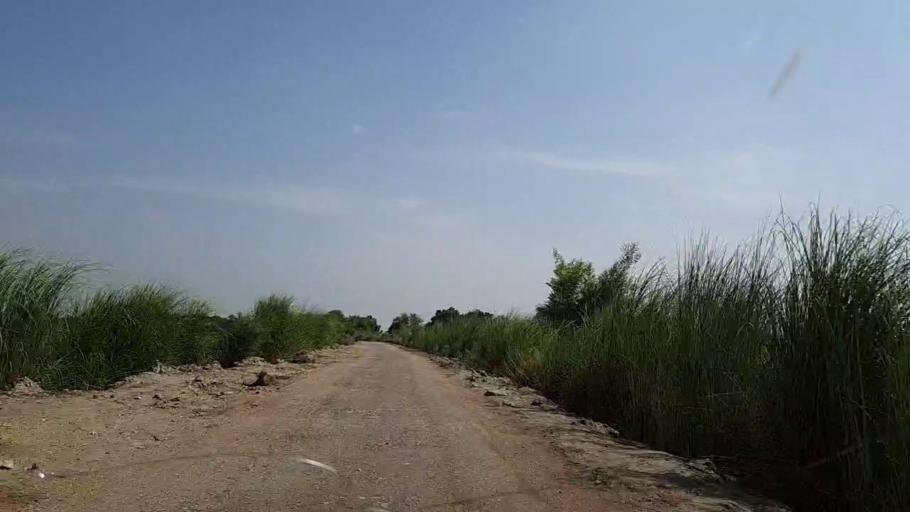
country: PK
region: Sindh
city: Khanpur
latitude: 27.7135
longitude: 69.3621
